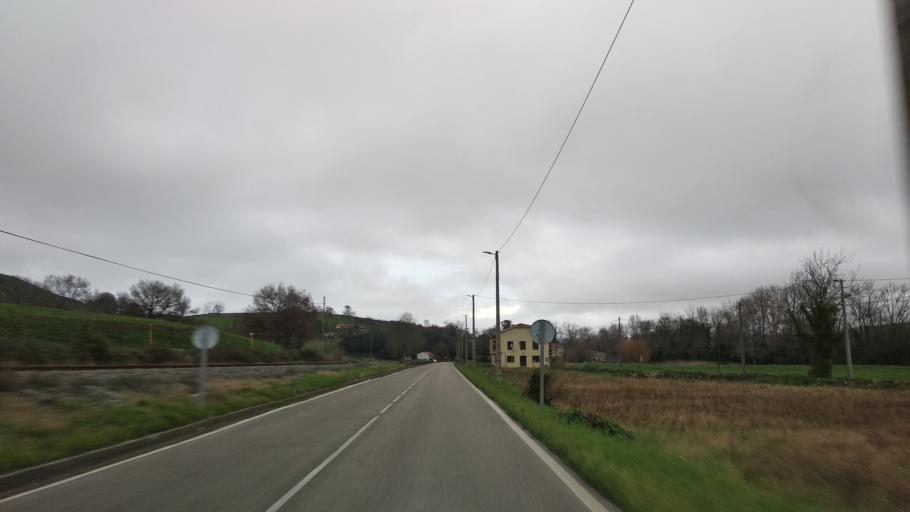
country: ES
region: Cantabria
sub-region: Provincia de Cantabria
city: Entrambasaguas
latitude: 43.4003
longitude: -3.7286
